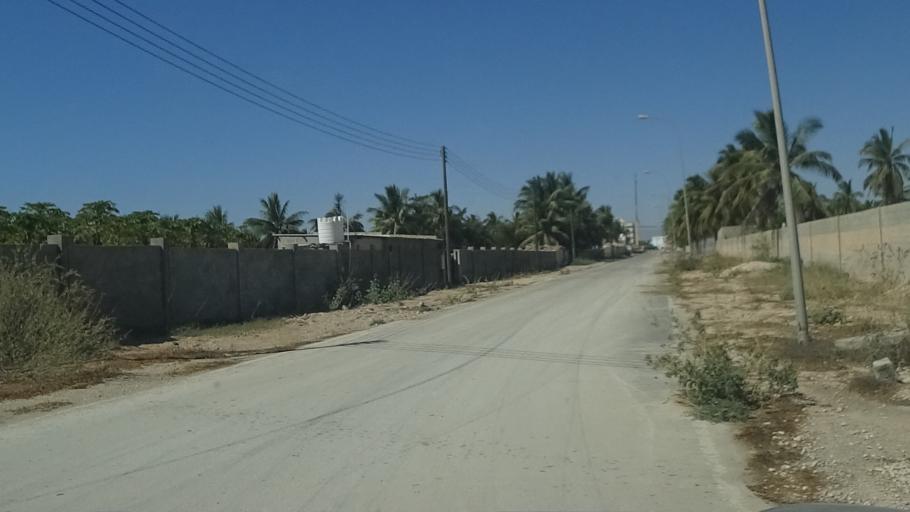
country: OM
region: Zufar
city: Salalah
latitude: 17.0288
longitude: 54.1648
